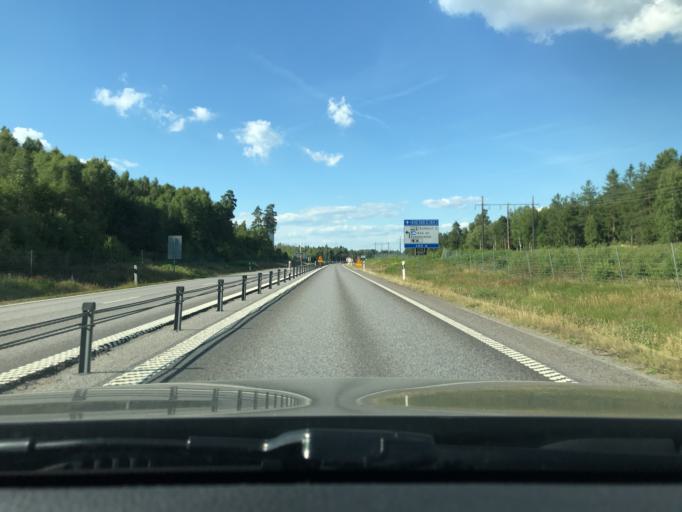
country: SE
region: Kronoberg
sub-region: Almhults Kommun
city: AElmhult
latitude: 56.5277
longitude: 14.1419
